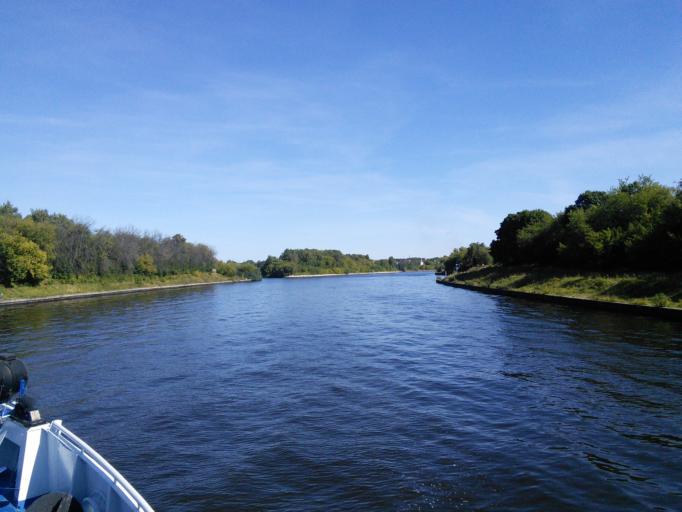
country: RU
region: Moskovskaya
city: Dolgoprudnyy
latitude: 55.9541
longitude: 37.4827
